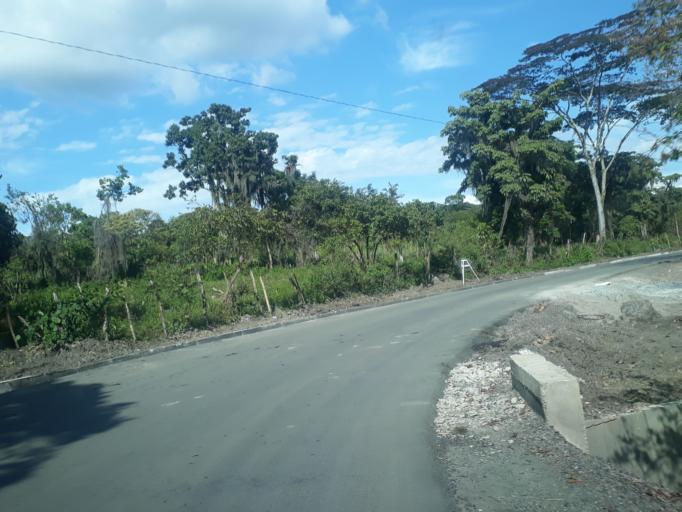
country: CO
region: Santander
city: Velez
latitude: 6.0590
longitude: -73.6426
